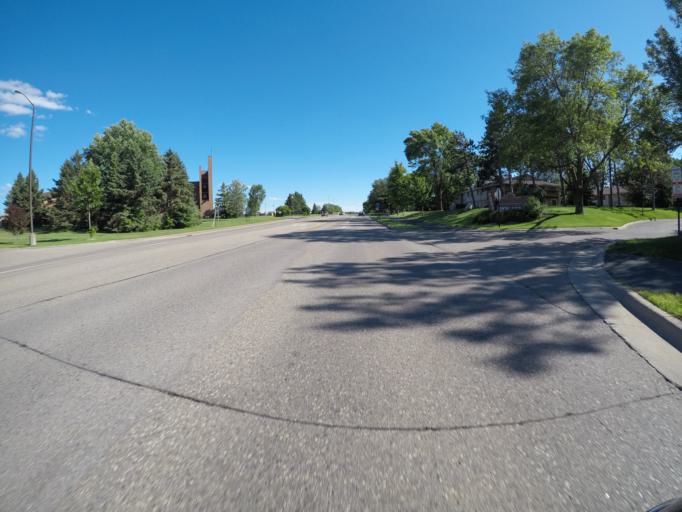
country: US
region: Minnesota
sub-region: Hennepin County
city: Maple Grove
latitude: 45.0857
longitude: -93.4314
